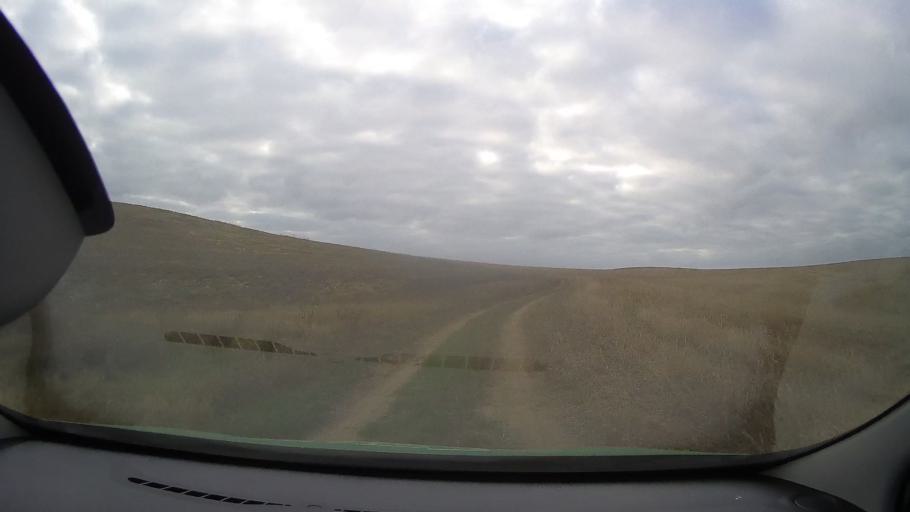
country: RO
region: Tulcea
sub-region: Comuna Jurilovca
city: Jurilovca
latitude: 44.7669
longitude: 28.9219
